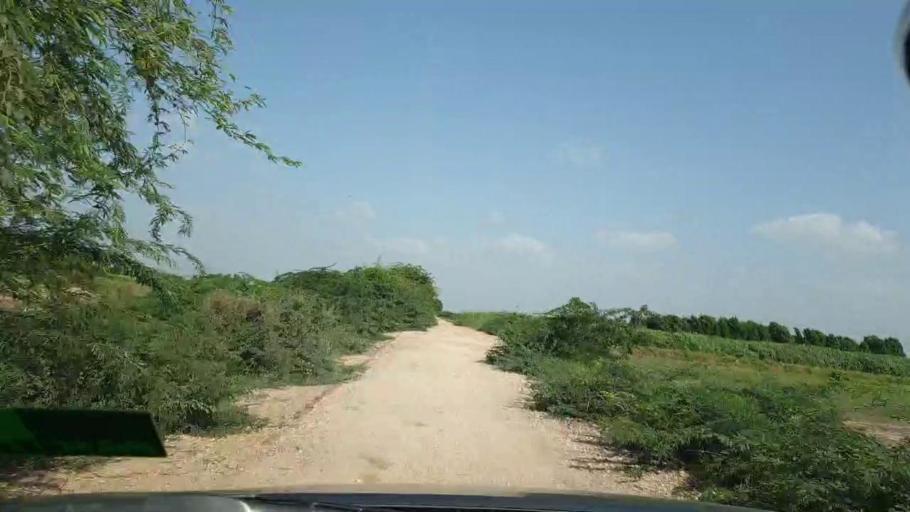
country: PK
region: Sindh
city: Tando Bago
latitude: 24.6827
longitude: 69.1997
